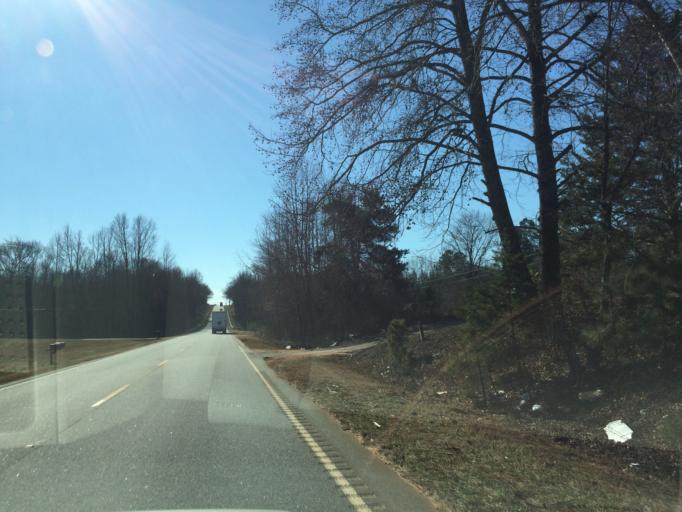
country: US
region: South Carolina
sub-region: Anderson County
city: Williamston
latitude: 34.6605
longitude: -82.5176
